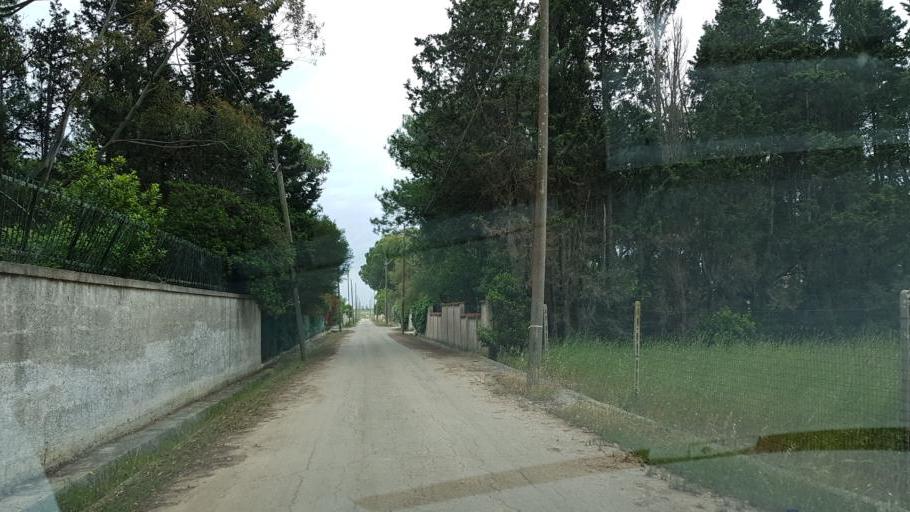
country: IT
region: Apulia
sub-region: Provincia di Brindisi
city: Brindisi
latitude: 40.6360
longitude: 17.8968
